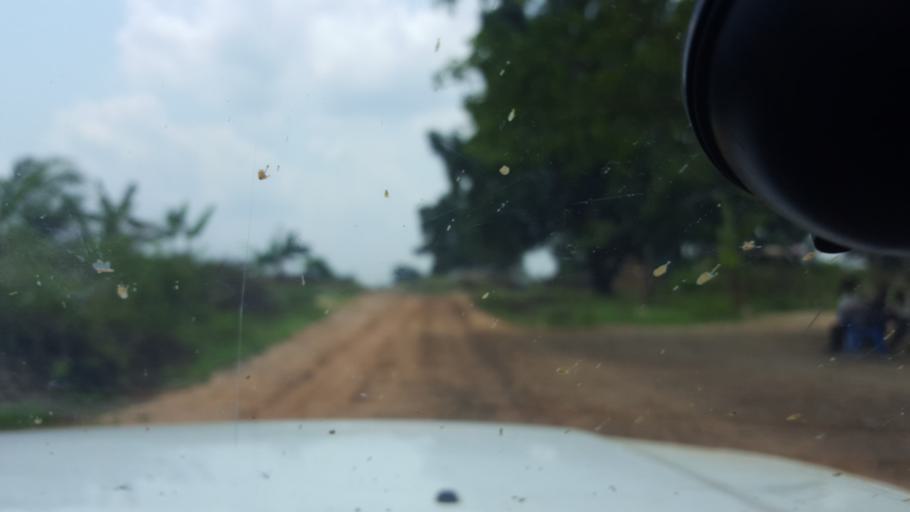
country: CD
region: Bandundu
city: Mushie
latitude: -3.7496
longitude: 16.6479
